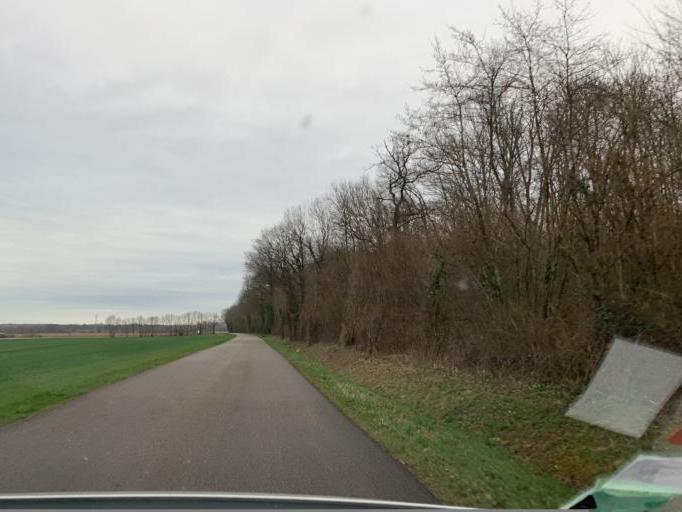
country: FR
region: Rhone-Alpes
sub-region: Departement de l'Ain
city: Mionnay
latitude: 45.8765
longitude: 4.9420
